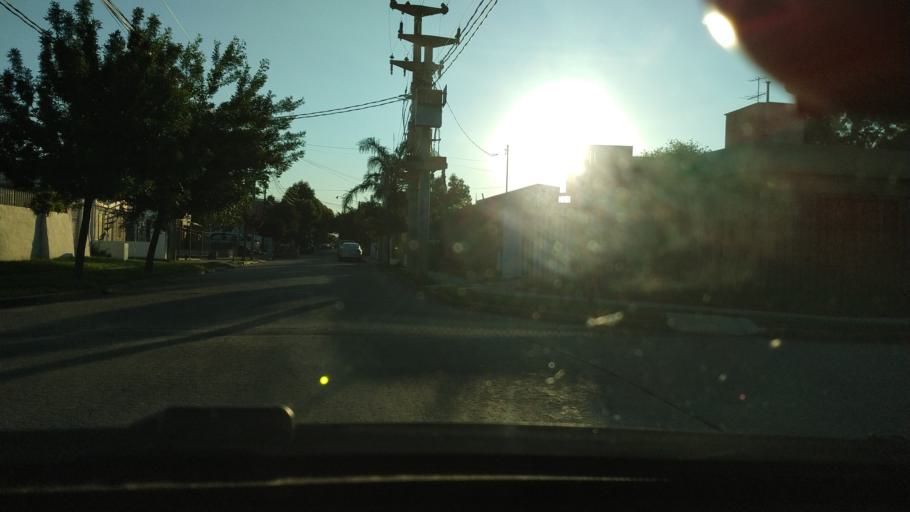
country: AR
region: Cordoba
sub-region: Departamento de Capital
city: Cordoba
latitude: -31.3650
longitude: -64.2289
